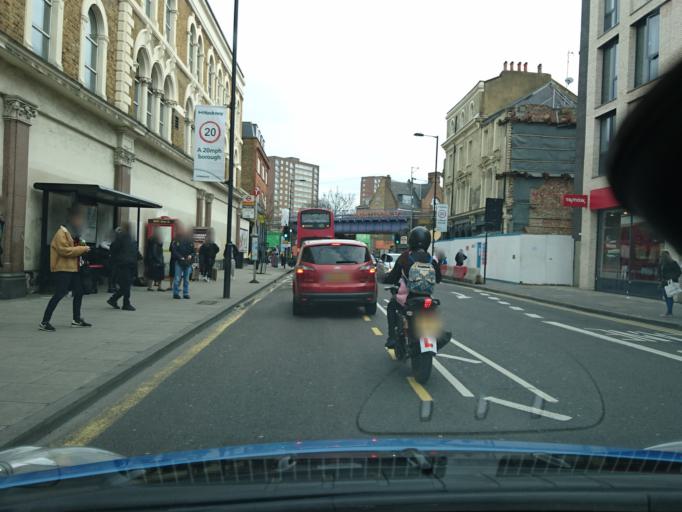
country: GB
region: England
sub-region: Greater London
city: Hackney
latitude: 51.5476
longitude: -0.0559
